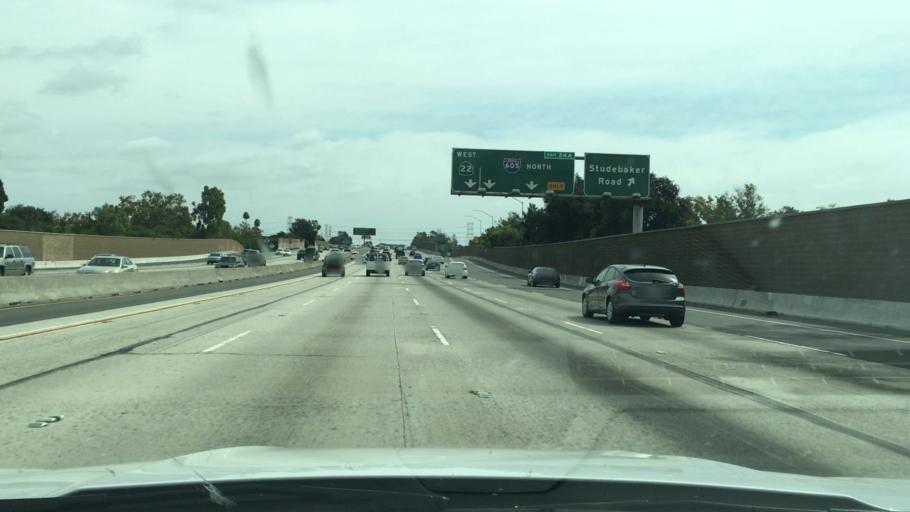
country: US
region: California
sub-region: Orange County
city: Rossmoor
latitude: 33.7932
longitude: -118.1031
